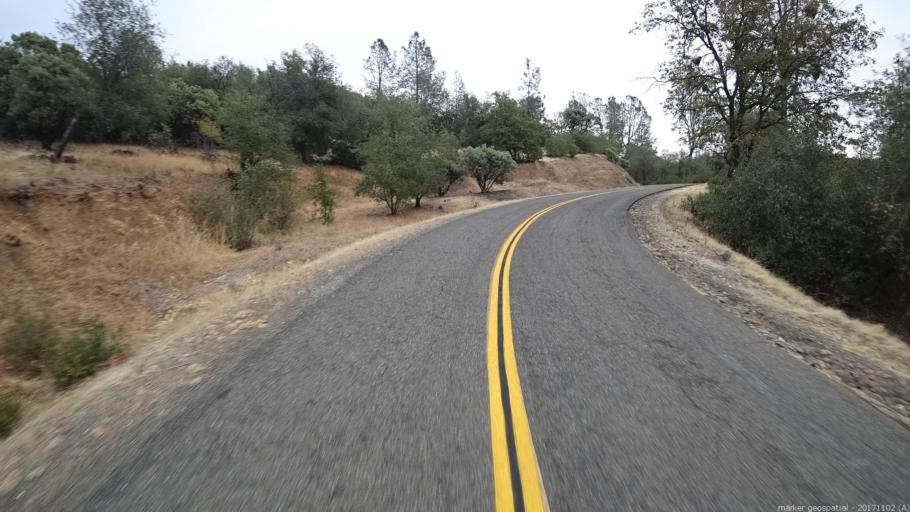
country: US
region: California
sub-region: Shasta County
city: Central Valley (historical)
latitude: 40.6584
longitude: -122.4293
